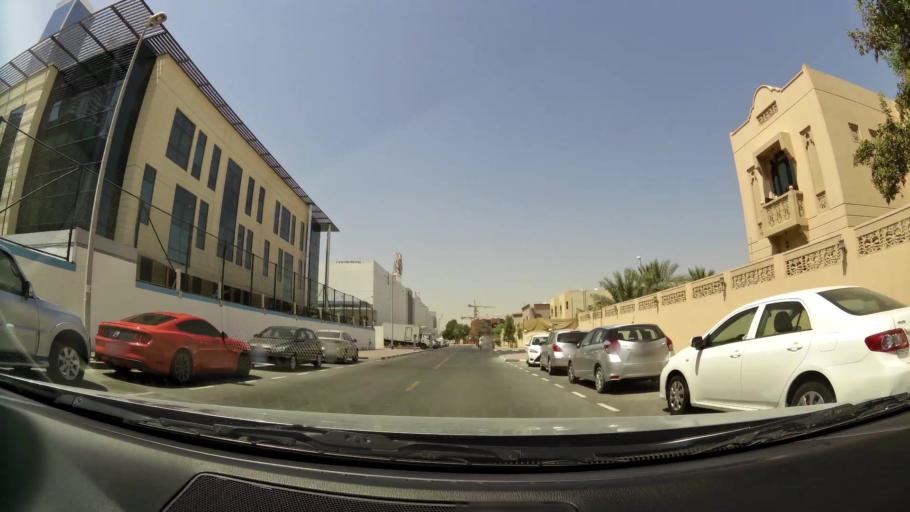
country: AE
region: Dubai
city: Dubai
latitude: 25.2114
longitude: 55.2710
